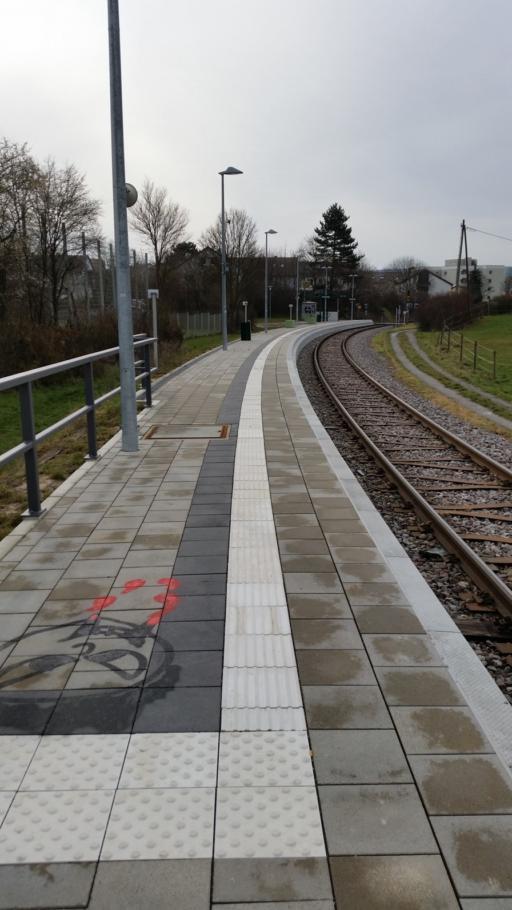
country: DE
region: Baden-Wuerttemberg
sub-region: Regierungsbezirk Stuttgart
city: Korntal
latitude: 48.8311
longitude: 9.1123
